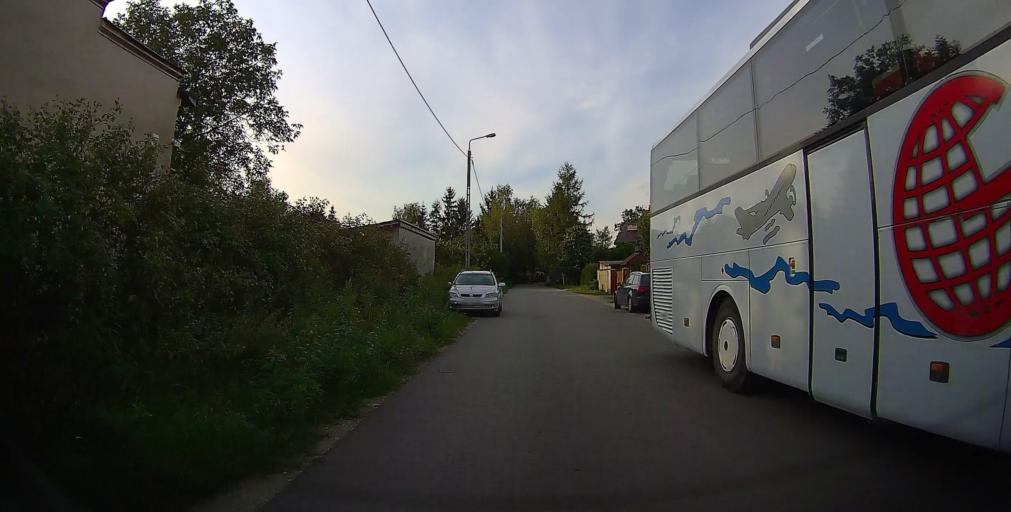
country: PL
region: Masovian Voivodeship
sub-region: Powiat piaseczynski
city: Piaseczno
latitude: 52.0647
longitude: 21.0164
